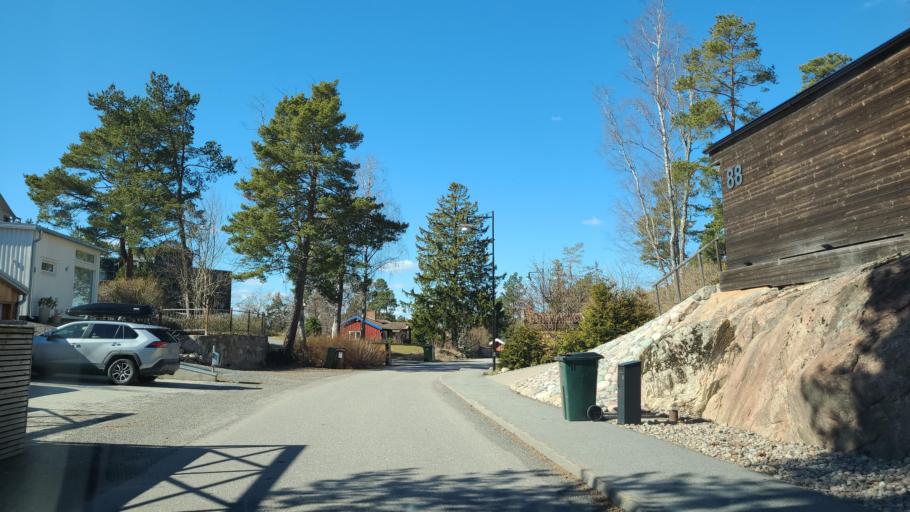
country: SE
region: Stockholm
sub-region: Lidingo
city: Brevik
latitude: 59.3271
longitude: 18.2228
